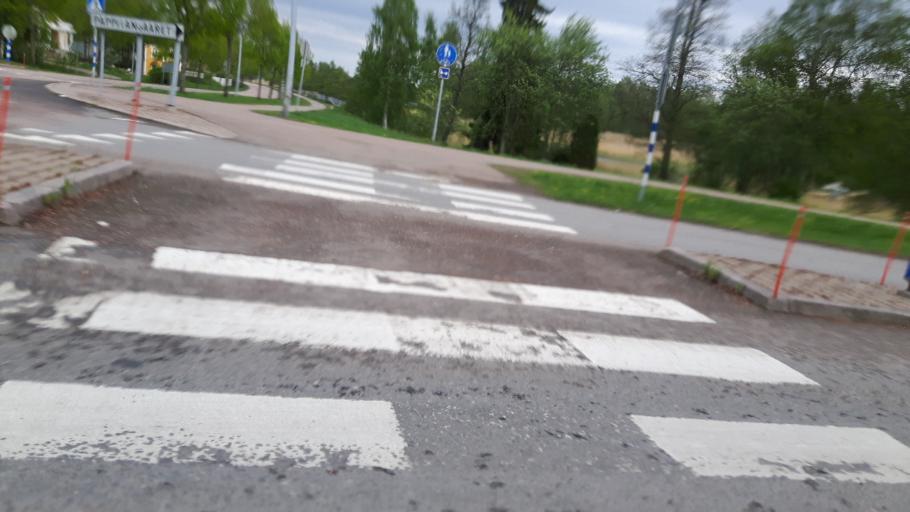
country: FI
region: Kymenlaakso
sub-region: Kotka-Hamina
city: Hamina
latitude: 60.5634
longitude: 27.2037
